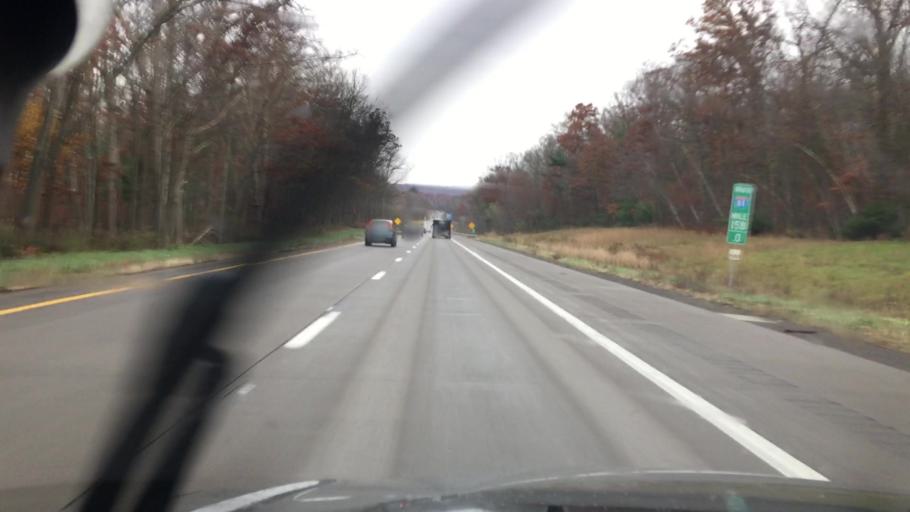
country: US
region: Pennsylvania
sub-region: Luzerne County
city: Nanticoke
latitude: 41.1303
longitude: -75.9621
